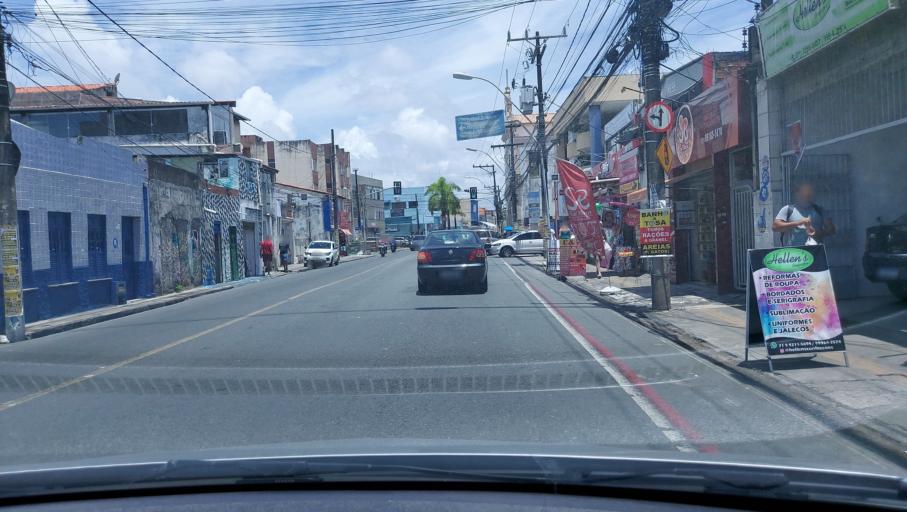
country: BR
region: Bahia
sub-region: Salvador
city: Salvador
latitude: -12.9897
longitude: -38.4827
